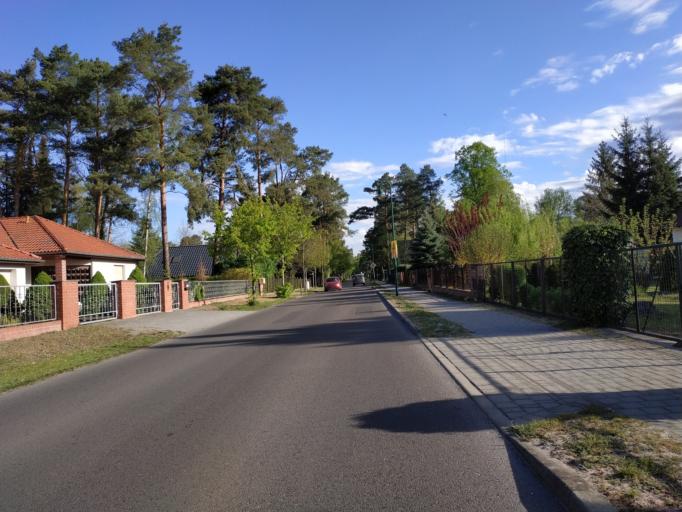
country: DE
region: Brandenburg
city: Petershagen
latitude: 52.5449
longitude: 13.8268
